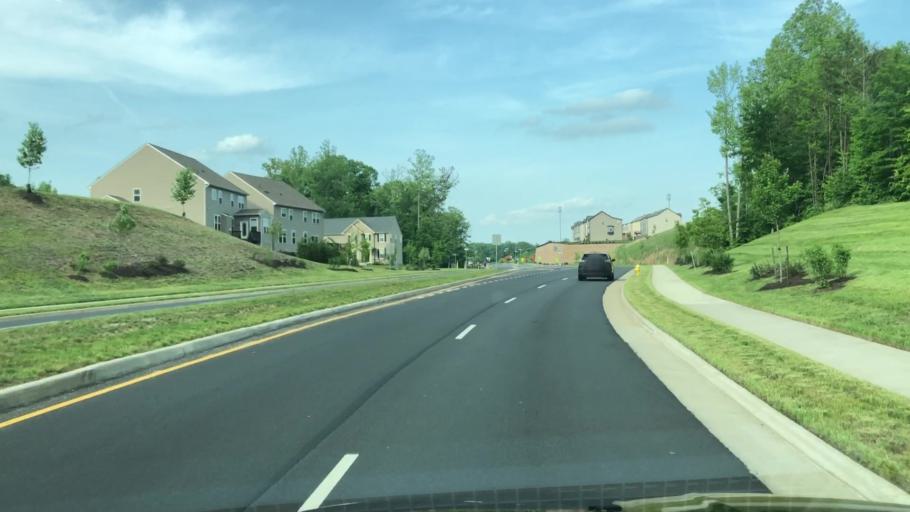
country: US
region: Virginia
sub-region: Stafford County
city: Stafford
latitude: 38.4327
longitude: -77.4595
